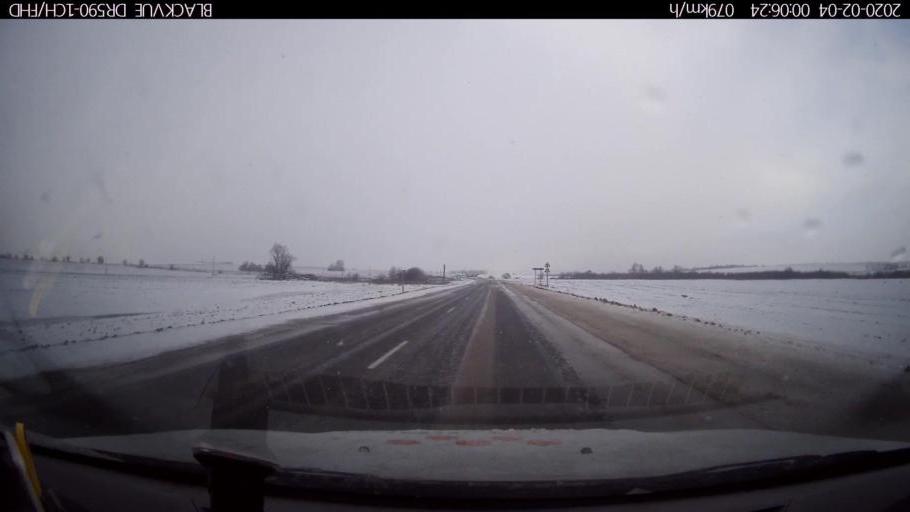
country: RU
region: Nizjnij Novgorod
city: Dal'neye Konstantinovo
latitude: 55.8478
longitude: 44.1281
